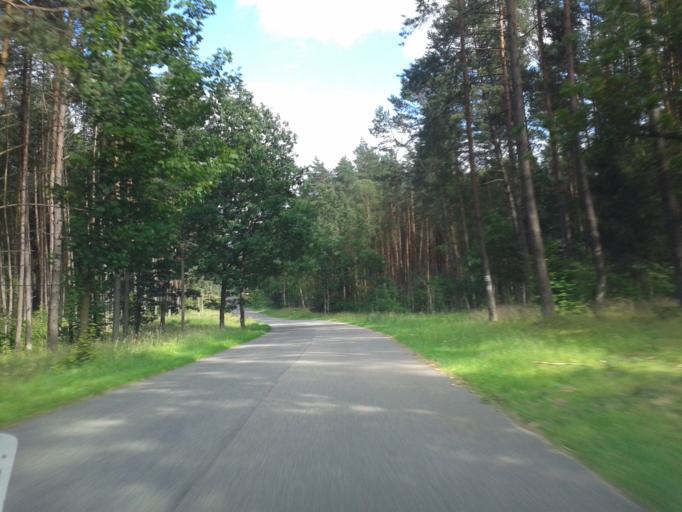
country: PL
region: West Pomeranian Voivodeship
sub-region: Powiat szczecinecki
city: Lubowo
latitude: 53.6340
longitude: 16.3362
